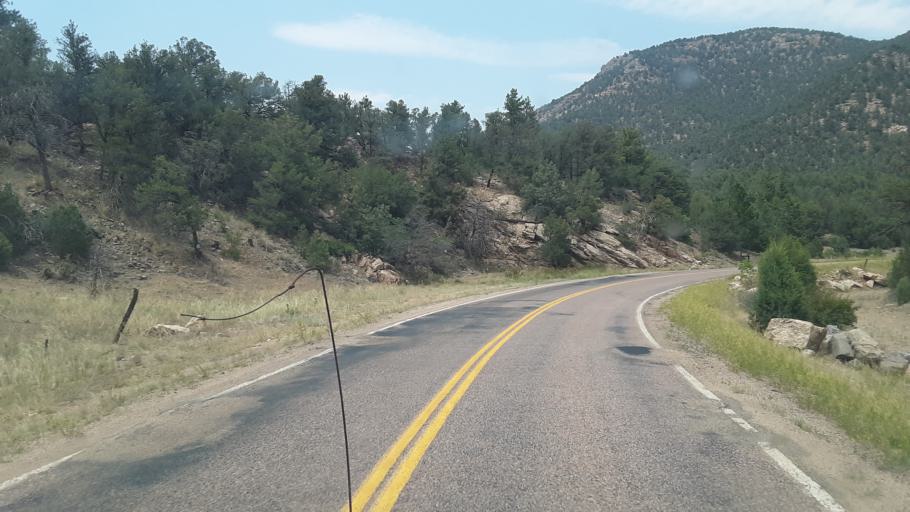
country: US
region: Colorado
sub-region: Fremont County
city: Canon City
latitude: 38.4112
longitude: -105.4372
